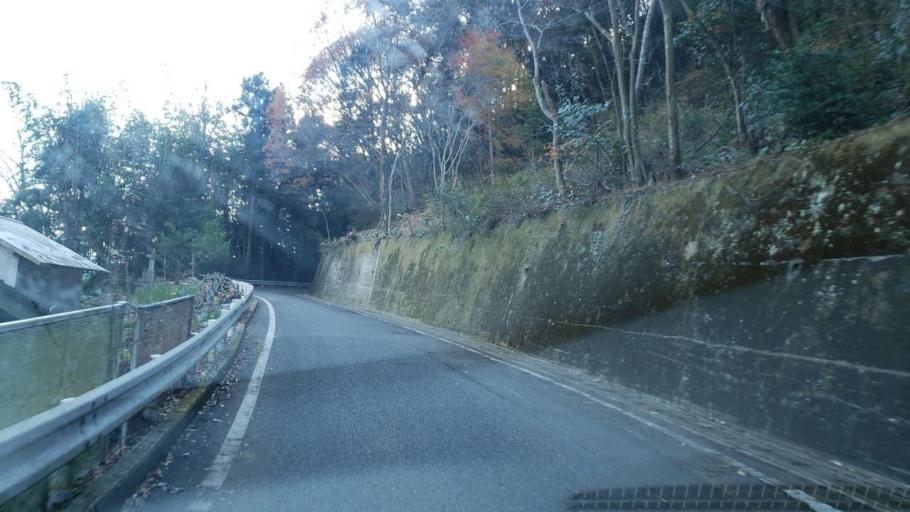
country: JP
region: Tokushima
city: Wakimachi
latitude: 34.1122
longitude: 134.0784
